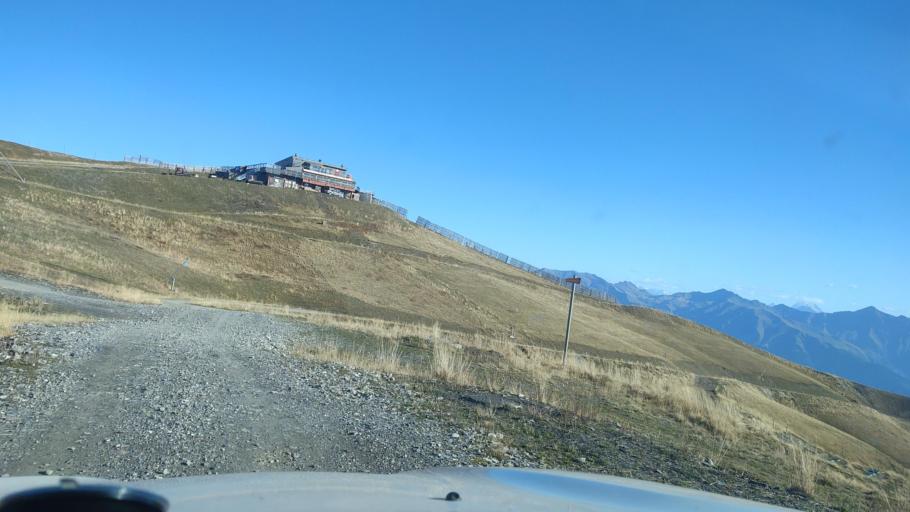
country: FR
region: Rhone-Alpes
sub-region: Departement de la Savoie
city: Saint-Etienne-de-Cuines
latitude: 45.2539
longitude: 6.2301
